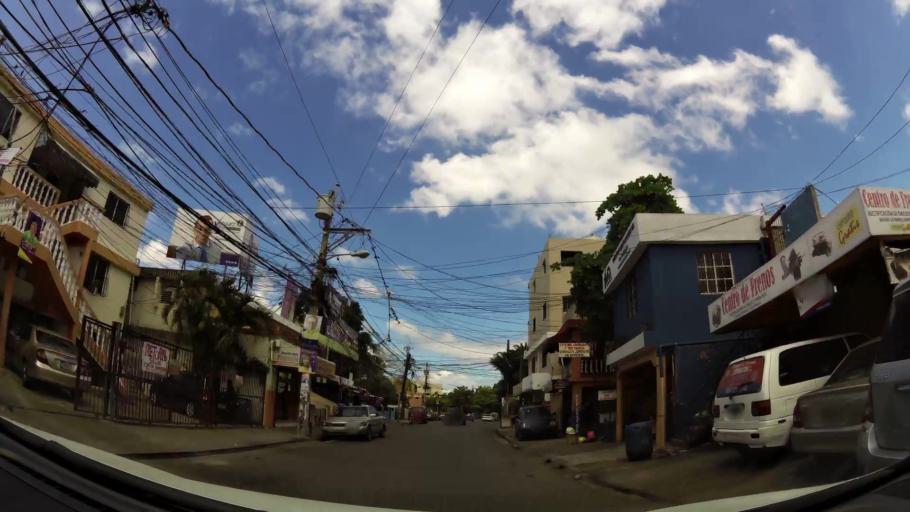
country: DO
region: Nacional
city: Bella Vista
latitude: 18.4674
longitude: -69.9478
